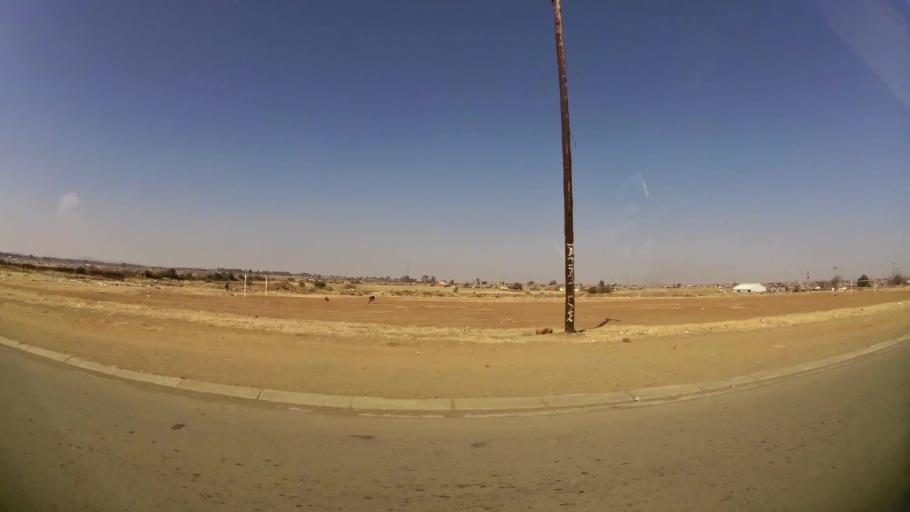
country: ZA
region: Orange Free State
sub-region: Mangaung Metropolitan Municipality
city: Bloemfontein
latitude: -29.1952
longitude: 26.2695
